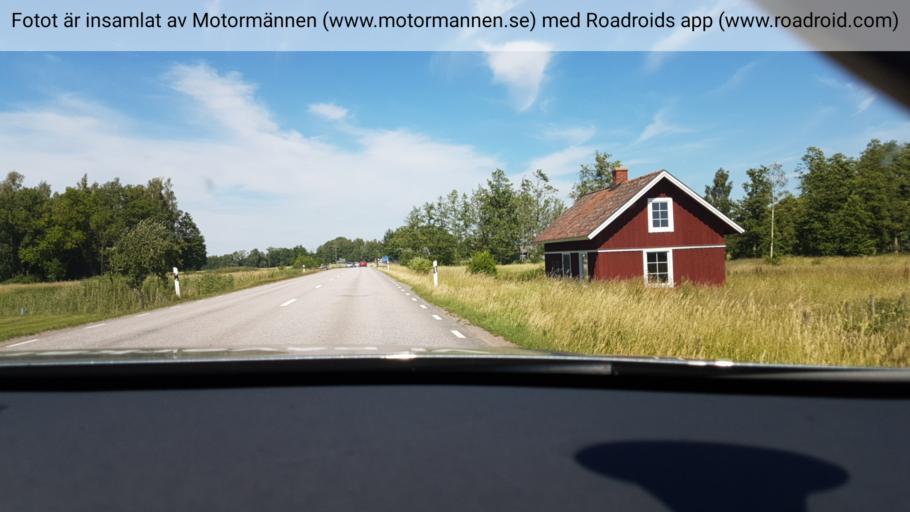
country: SE
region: Vaestra Goetaland
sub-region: Skovde Kommun
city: Stopen
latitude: 58.4834
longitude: 13.9582
